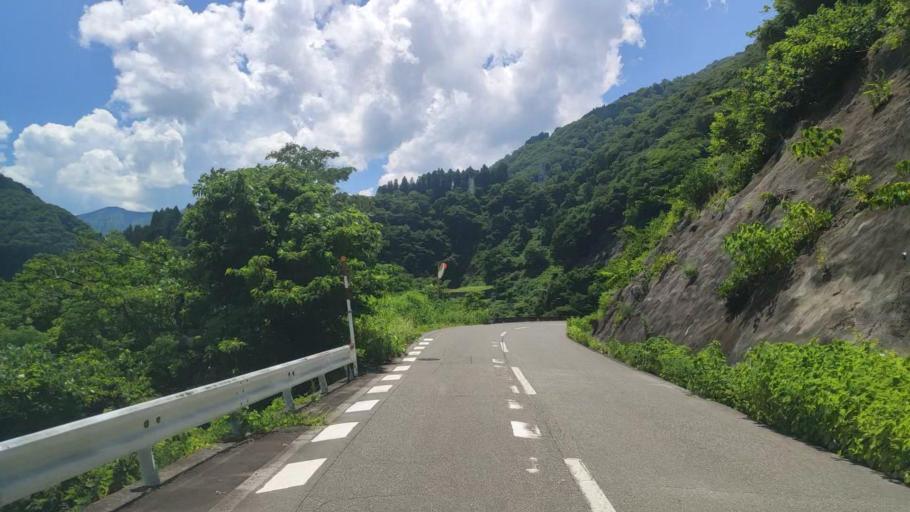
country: JP
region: Fukui
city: Ono
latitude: 35.8981
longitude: 136.5089
